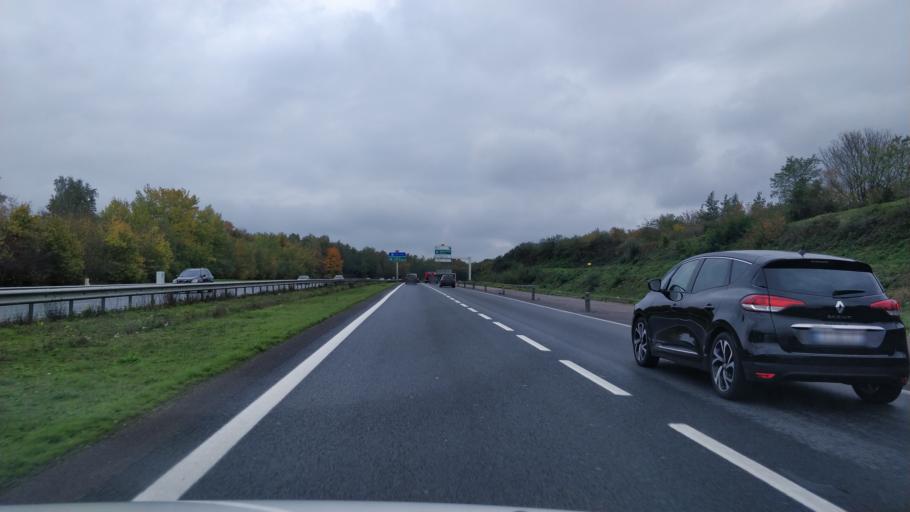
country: FR
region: Haute-Normandie
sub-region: Departement de la Seine-Maritime
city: Le Grand-Quevilly
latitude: 49.3911
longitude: 1.0414
